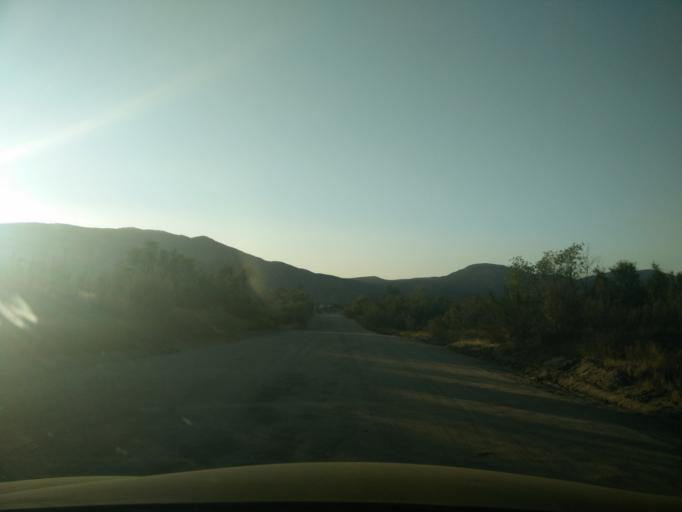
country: MX
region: Baja California
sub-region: Ensenada
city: Rancho Verde
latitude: 32.0541
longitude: -116.6456
